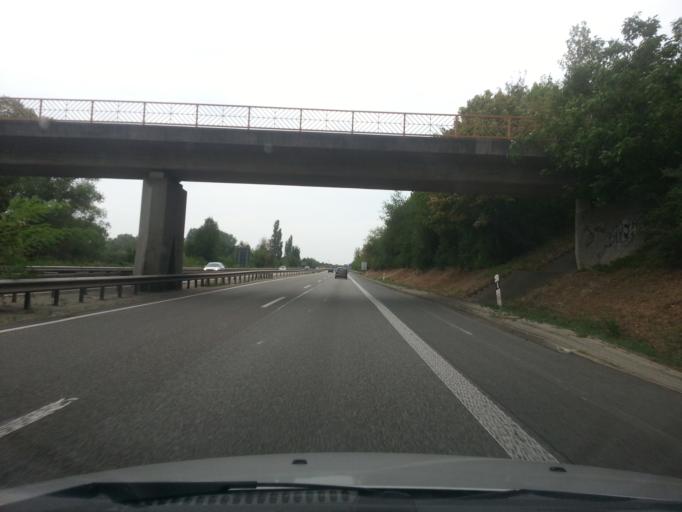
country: DE
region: Rheinland-Pfalz
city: Bornheim
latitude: 49.2032
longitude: 8.1480
